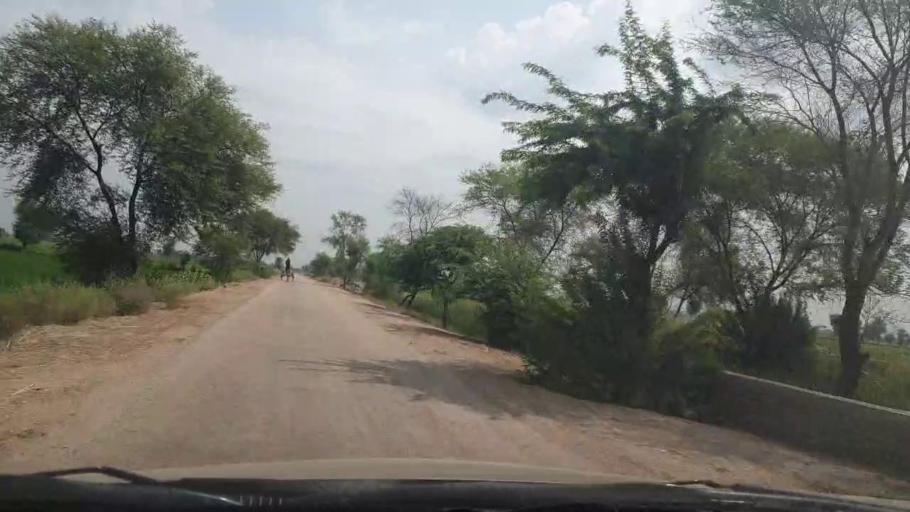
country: PK
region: Sindh
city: Miro Khan
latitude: 27.6940
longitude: 68.1981
